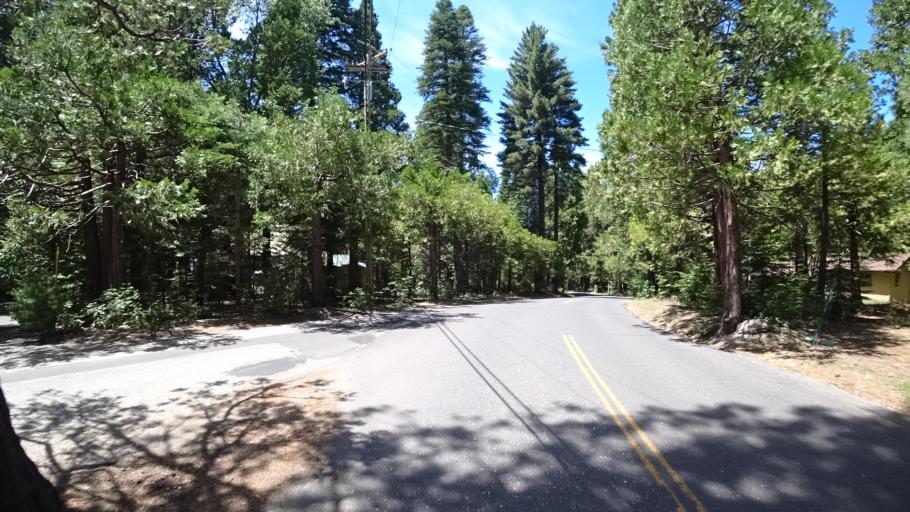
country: US
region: California
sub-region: Calaveras County
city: Arnold
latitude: 38.3001
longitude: -120.2746
